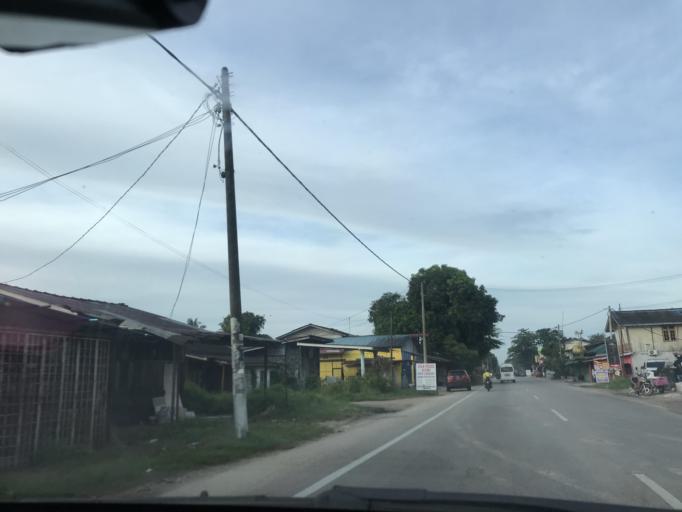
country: MY
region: Kelantan
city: Kota Bharu
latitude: 6.1043
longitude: 102.2114
